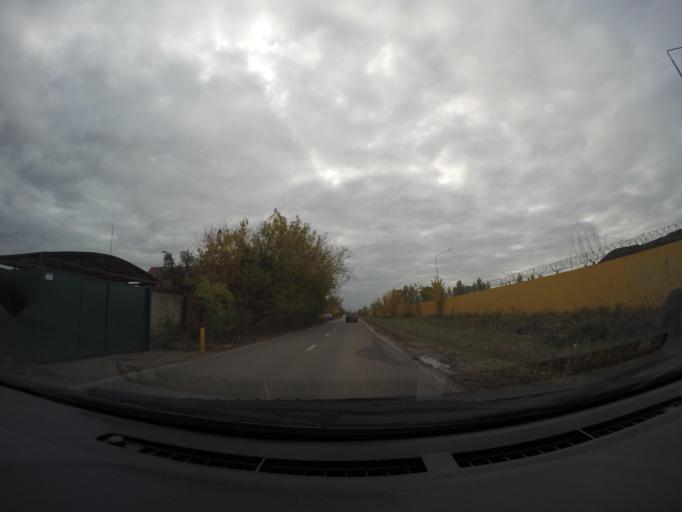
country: RU
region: Moskovskaya
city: Rechitsy
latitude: 55.6120
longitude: 38.4473
